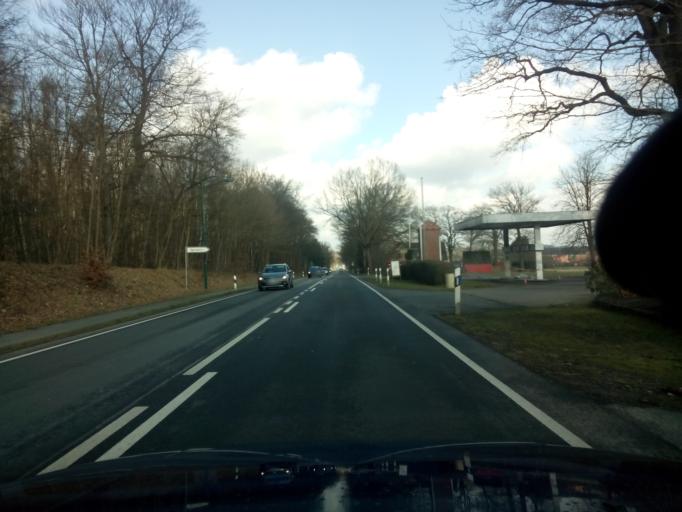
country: DE
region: Lower Saxony
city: Hambergen
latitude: 53.2931
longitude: 8.8319
